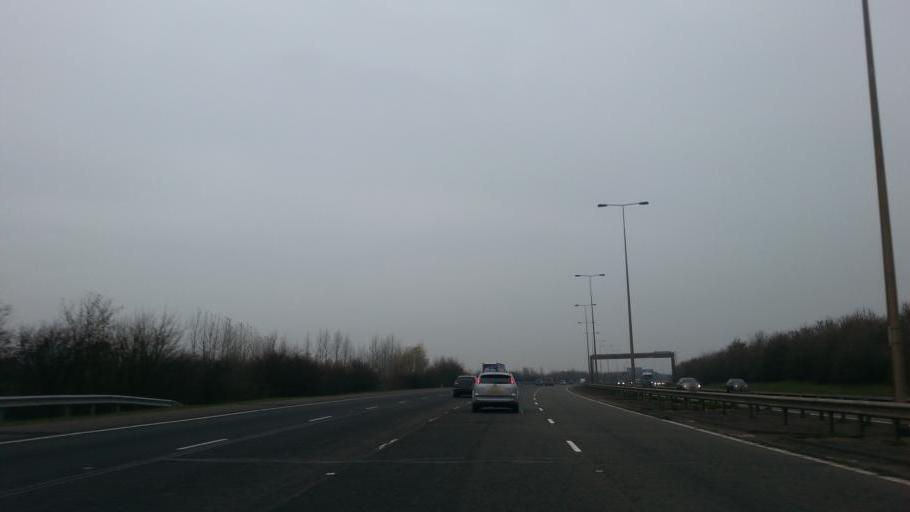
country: GB
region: England
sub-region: Cambridgeshire
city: Stilton
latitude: 52.4781
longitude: -0.2869
